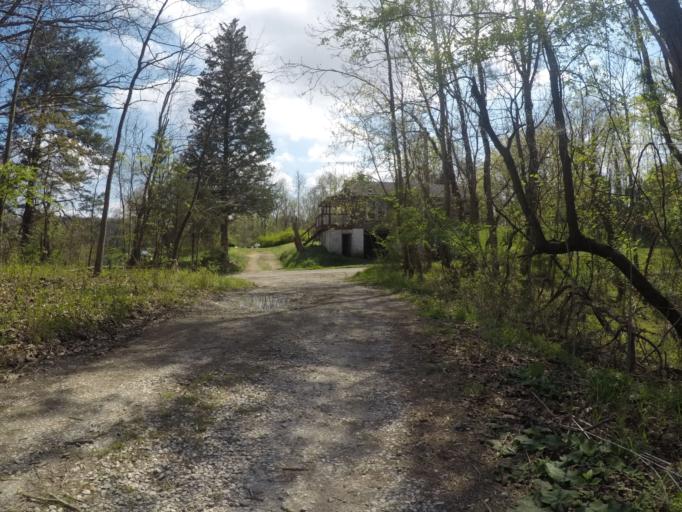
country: US
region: West Virginia
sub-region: Wayne County
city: Ceredo
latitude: 38.3874
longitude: -82.5408
